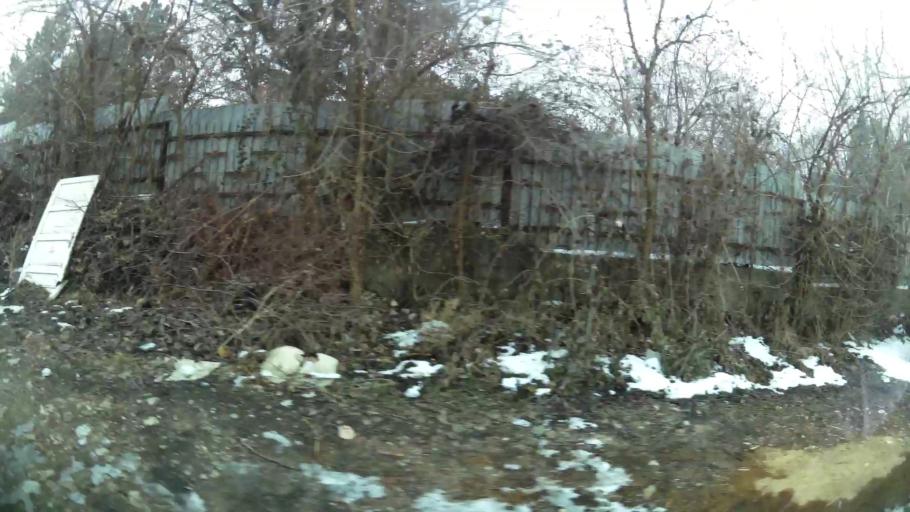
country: MK
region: Suto Orizari
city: Suto Orizare
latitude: 42.0348
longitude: 21.4329
